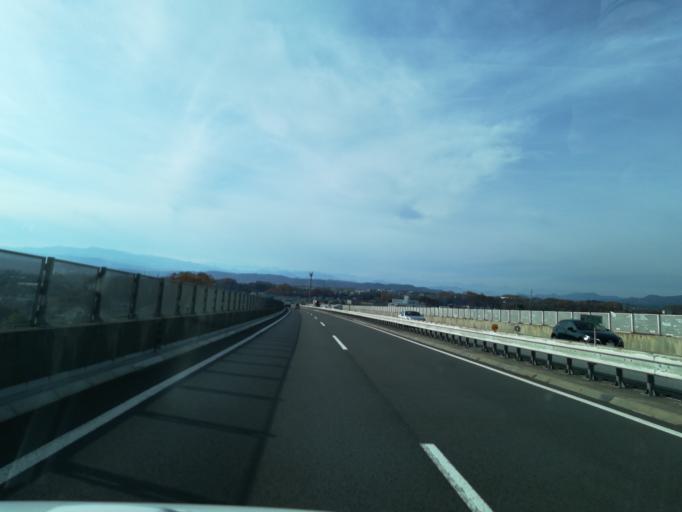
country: JP
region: Nagano
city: Saku
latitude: 36.2781
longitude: 138.5062
